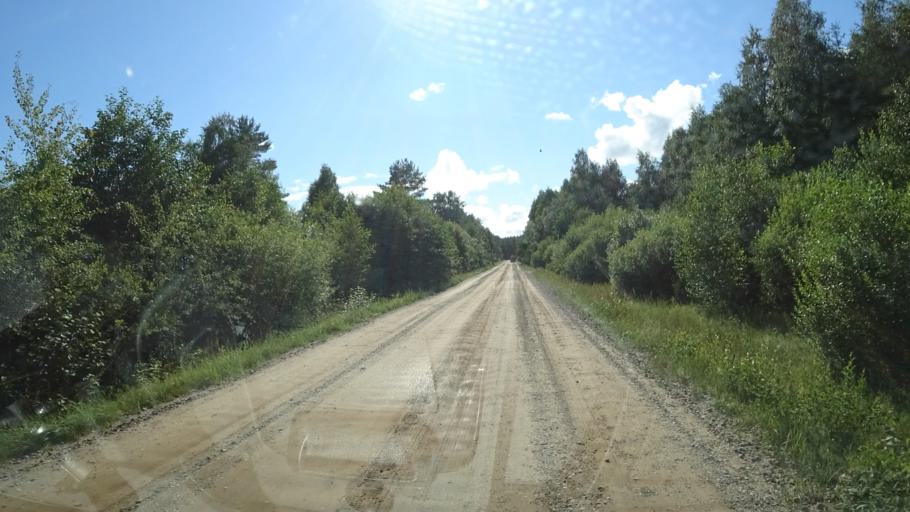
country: LV
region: Ventspils
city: Ventspils
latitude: 57.4879
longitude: 21.6583
